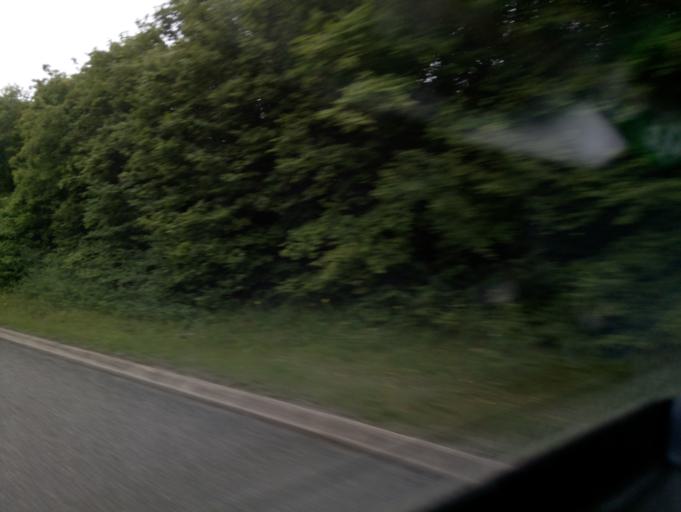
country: GB
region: England
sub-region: Worcestershire
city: Droitwich
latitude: 52.2620
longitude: -2.1782
